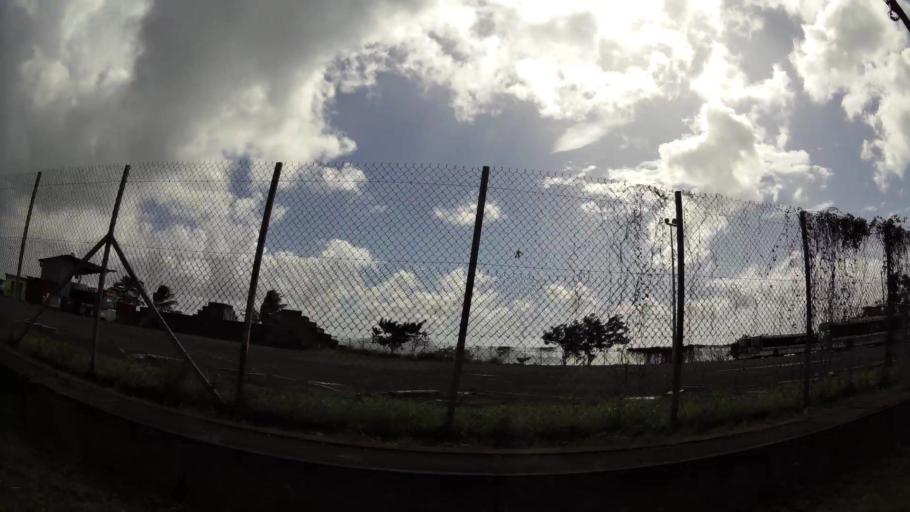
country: MQ
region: Martinique
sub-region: Martinique
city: Fort-de-France
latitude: 14.6016
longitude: -61.0779
